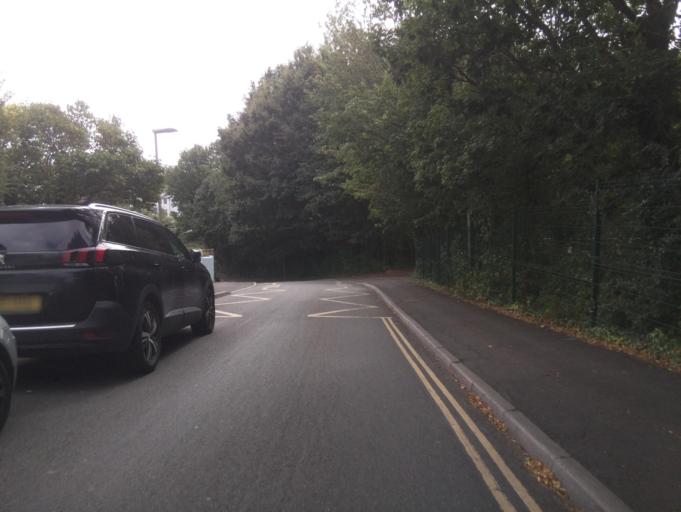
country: GB
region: England
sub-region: Devon
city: Totnes
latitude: 50.4288
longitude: -3.6757
